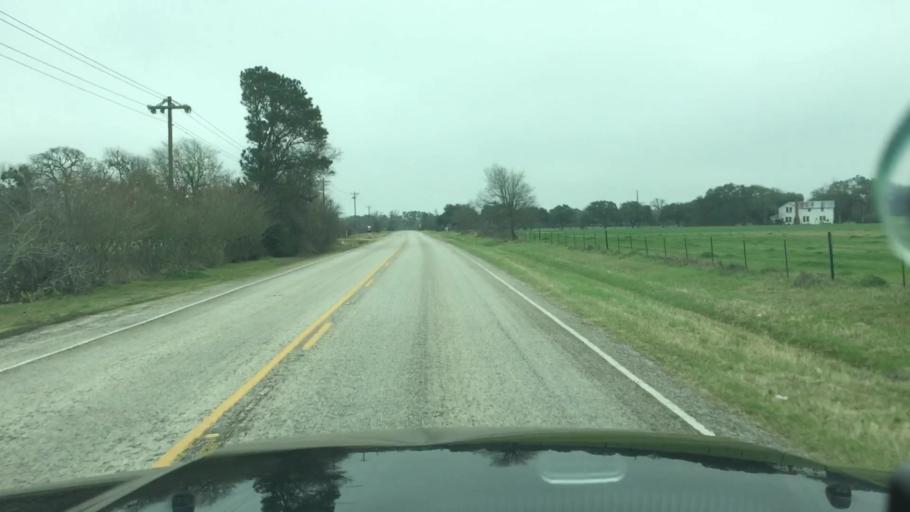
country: US
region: Texas
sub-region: Fayette County
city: La Grange
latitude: 30.0051
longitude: -96.9033
